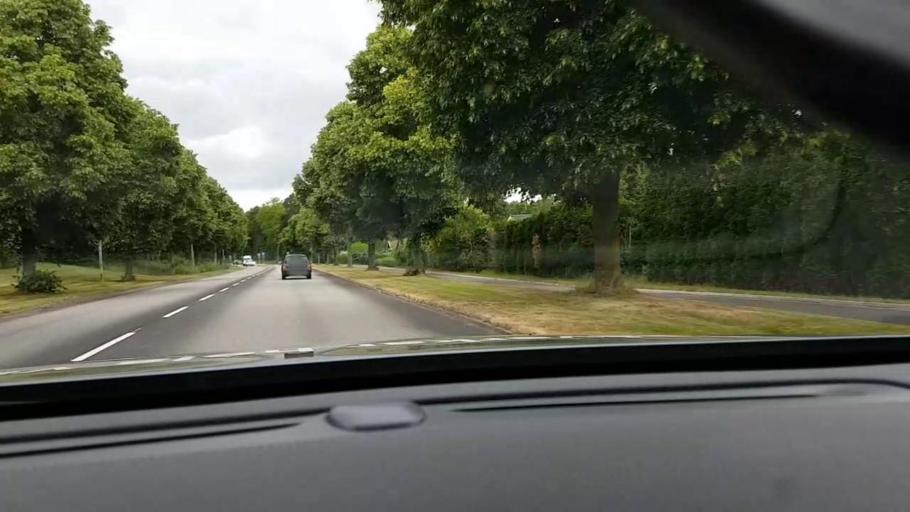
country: SE
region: Skane
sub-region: Hassleholms Kommun
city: Hassleholm
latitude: 56.1707
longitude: 13.7798
